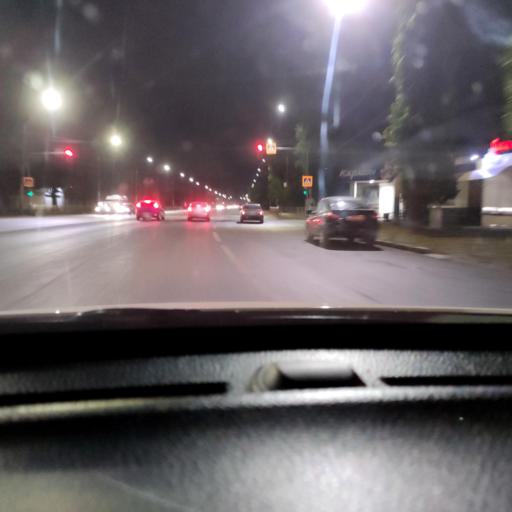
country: RU
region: Voronezj
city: Somovo
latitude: 51.7080
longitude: 39.2767
